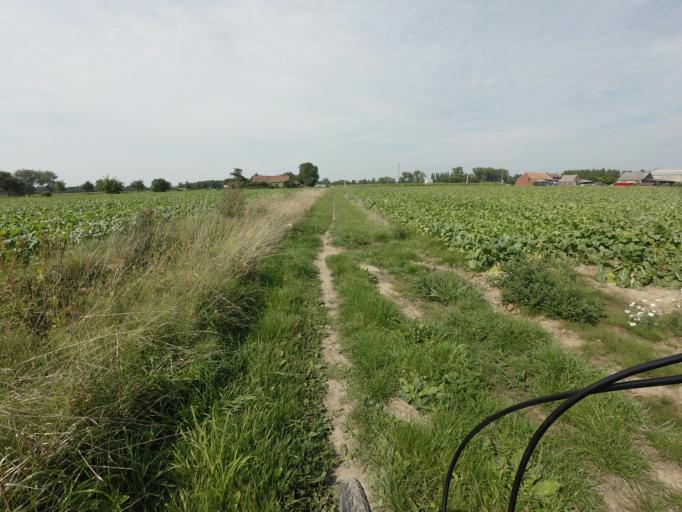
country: BE
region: Flanders
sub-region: Provincie Vlaams-Brabant
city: Zemst
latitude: 50.9642
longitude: 4.4734
